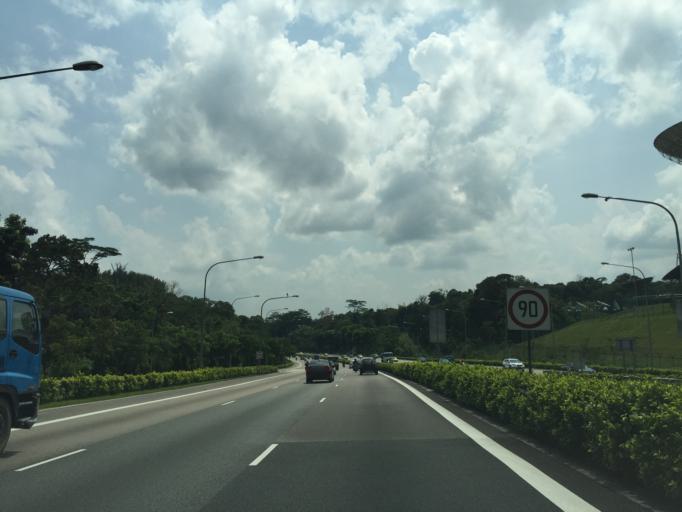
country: SG
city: Singapore
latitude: 1.3498
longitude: 103.7912
